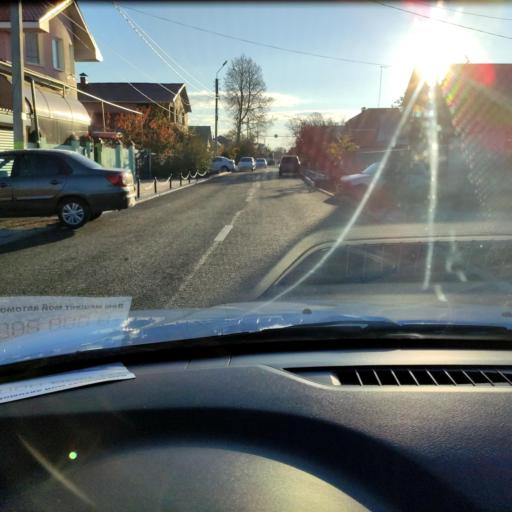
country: RU
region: Samara
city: Tol'yatti
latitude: 53.5284
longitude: 49.4258
